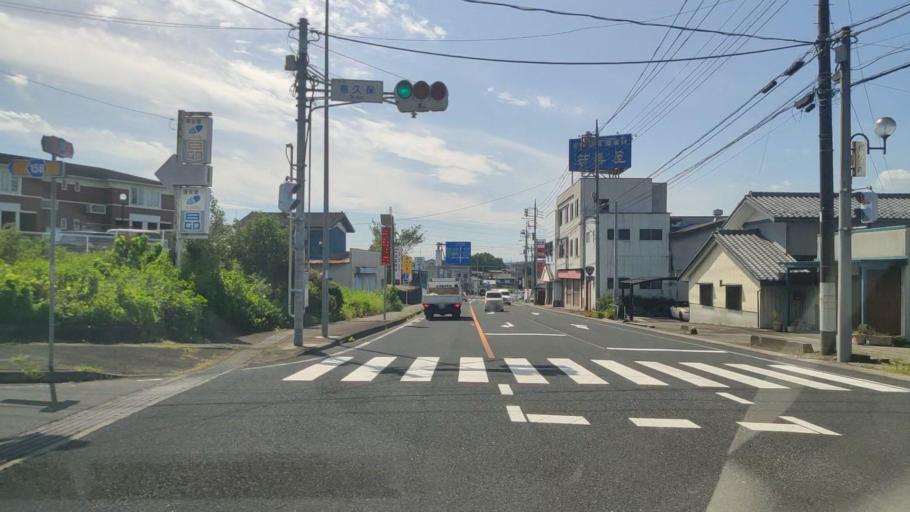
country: JP
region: Gunma
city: Shibukawa
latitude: 36.5215
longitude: 139.0112
